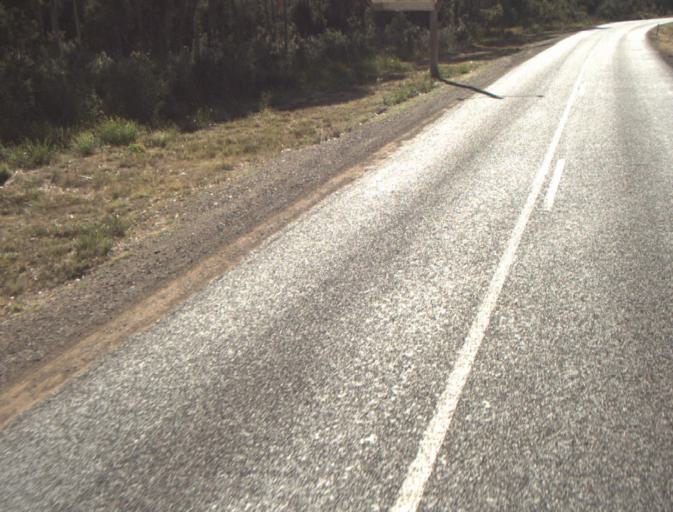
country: AU
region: Tasmania
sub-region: Launceston
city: Mayfield
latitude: -41.3345
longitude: 147.1416
